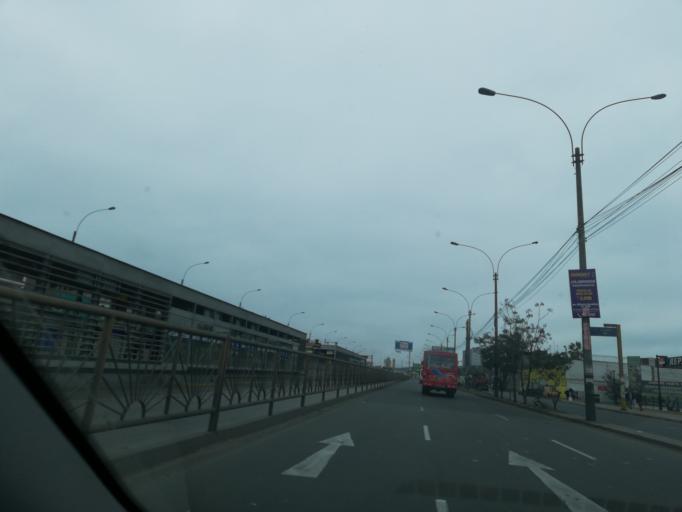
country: PE
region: Lima
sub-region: Lima
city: Independencia
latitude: -11.9893
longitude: -77.0571
